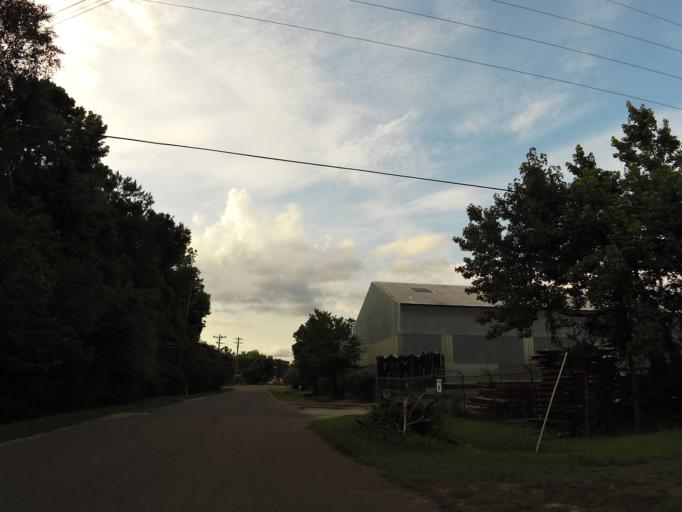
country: US
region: Florida
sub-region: Duval County
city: Jacksonville
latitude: 30.3210
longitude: -81.7667
